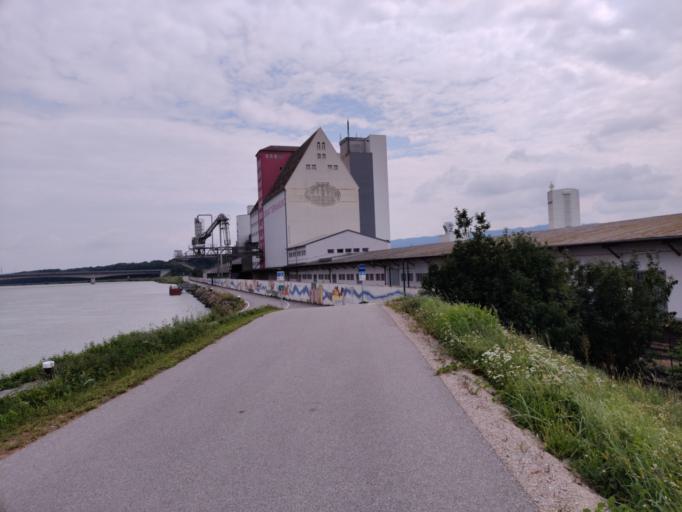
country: AT
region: Lower Austria
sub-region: Politischer Bezirk Melk
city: Klein-Poechlarn
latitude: 48.2132
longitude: 15.2217
